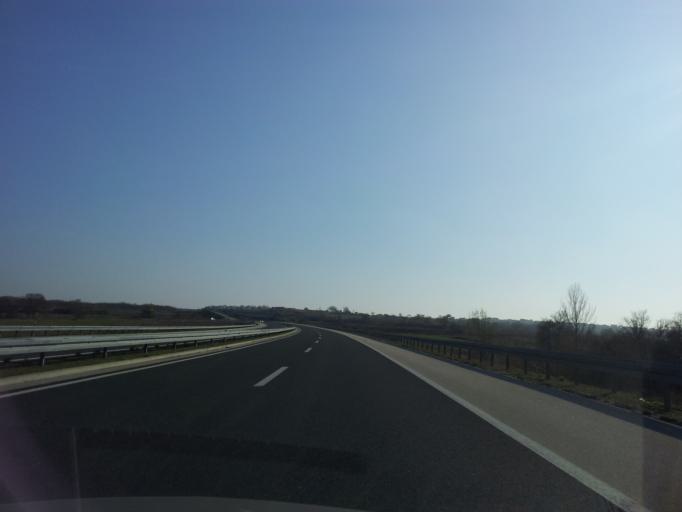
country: HR
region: Zadarska
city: Policnik
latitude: 44.1674
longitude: 15.4206
